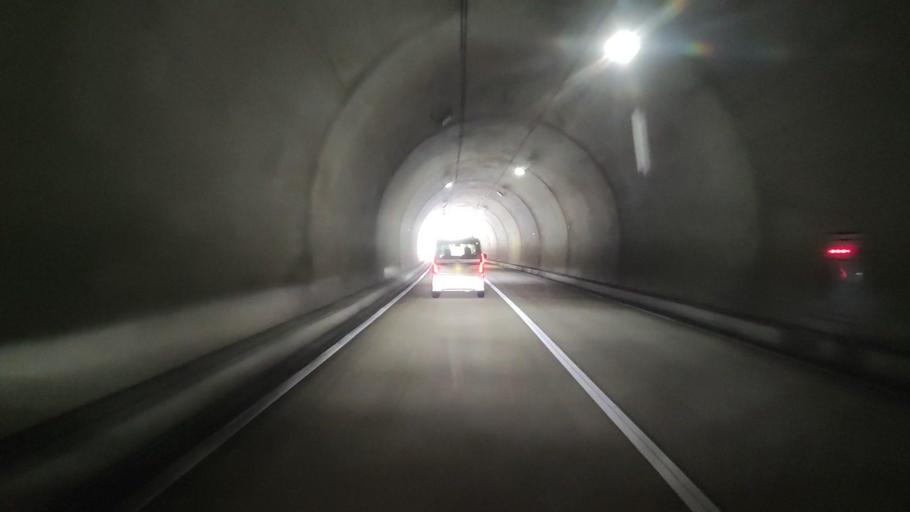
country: JP
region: Wakayama
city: Shingu
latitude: 33.8880
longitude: 135.8796
